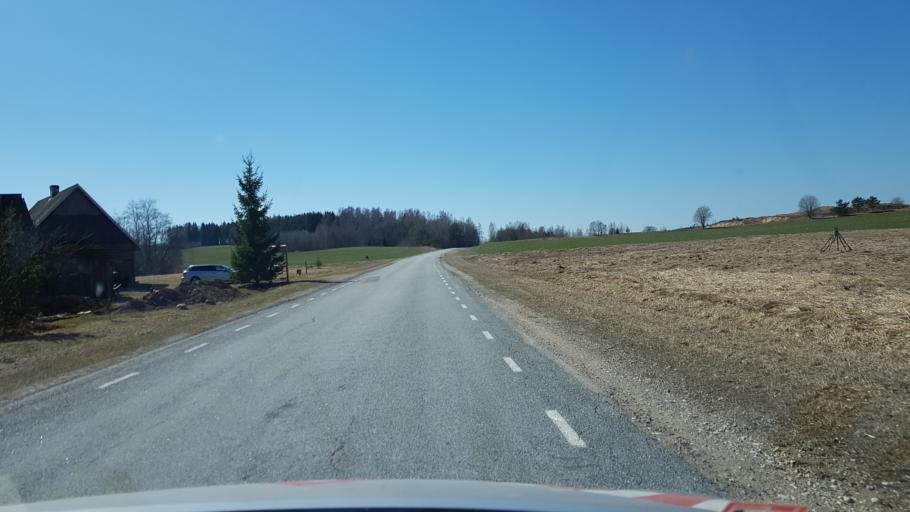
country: EE
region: Laeaene-Virumaa
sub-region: Rakke vald
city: Rakke
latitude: 59.0093
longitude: 26.3328
